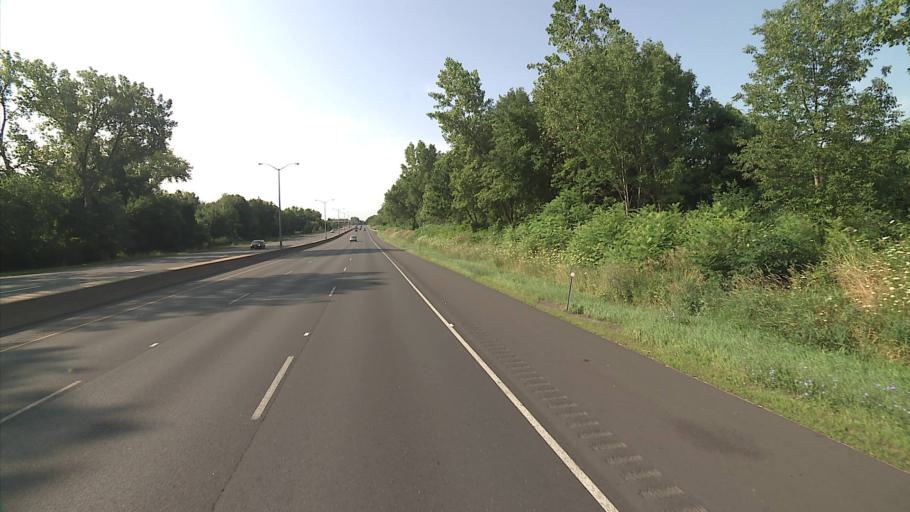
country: US
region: Connecticut
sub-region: Hartford County
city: Enfield
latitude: 41.9838
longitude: -72.5886
